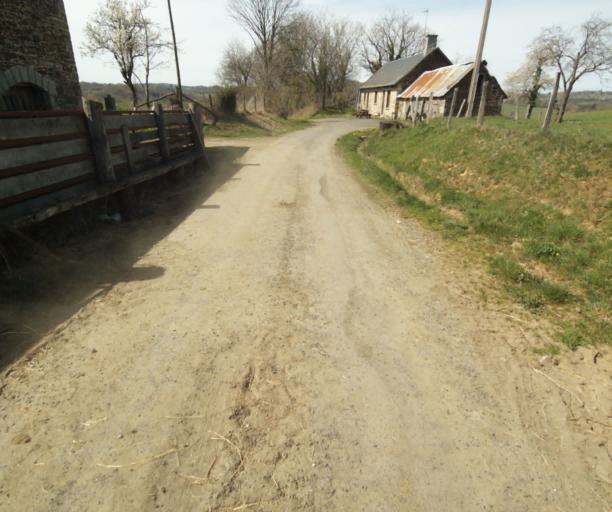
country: FR
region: Limousin
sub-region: Departement de la Correze
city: Naves
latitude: 45.3699
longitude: 1.7743
